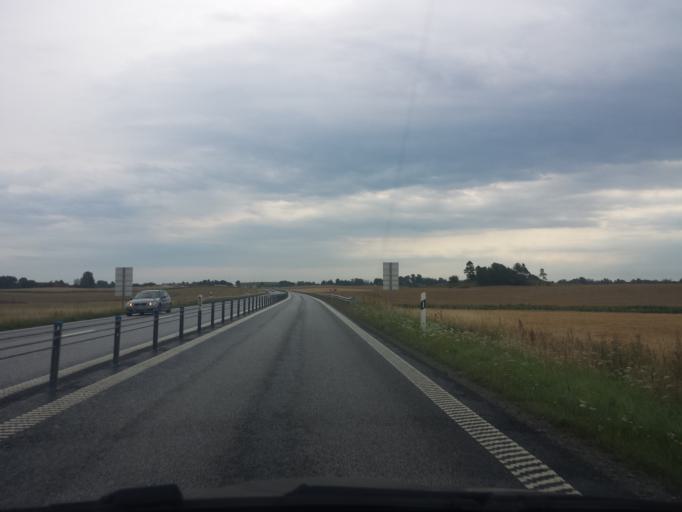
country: SE
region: Skane
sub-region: Skurups Kommun
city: Rydsgard
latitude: 55.4843
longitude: 13.5762
